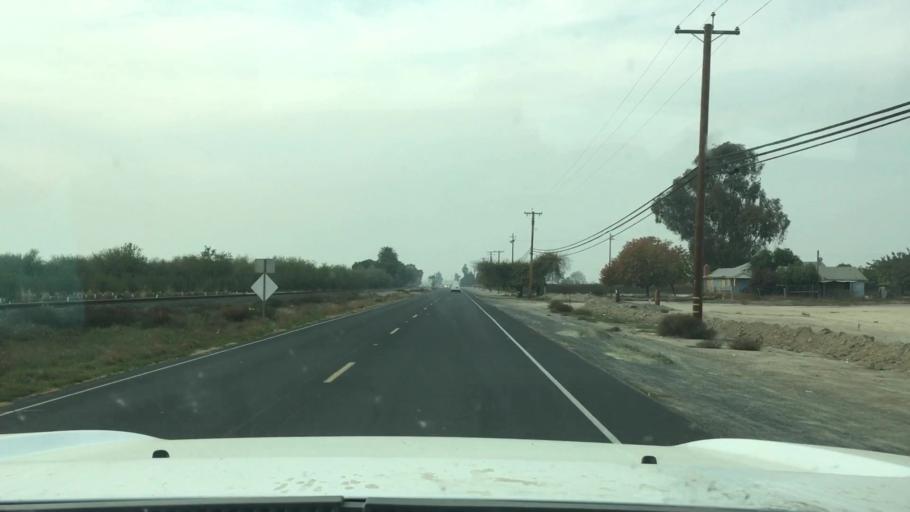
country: US
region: California
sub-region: San Joaquin County
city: Manteca
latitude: 37.8486
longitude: -121.1885
